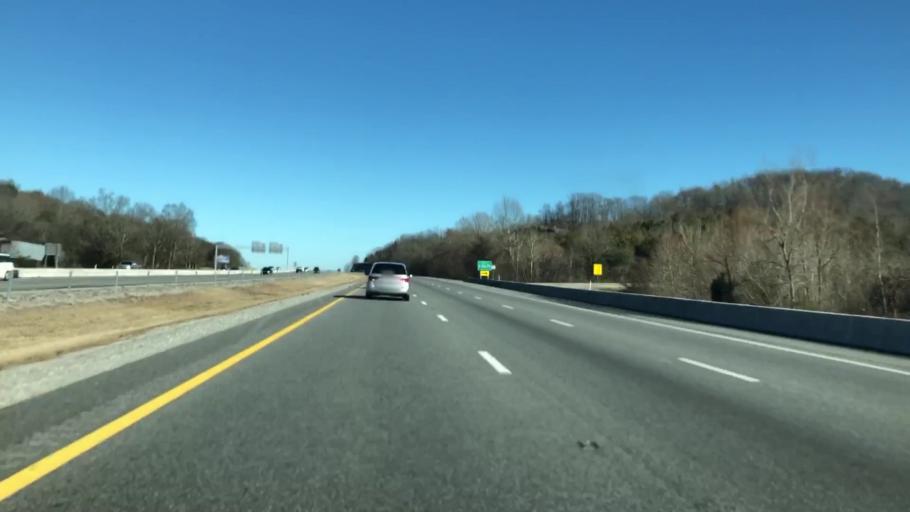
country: US
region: Tennessee
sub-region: Williamson County
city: Thompson's Station
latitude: 35.8228
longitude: -86.8377
